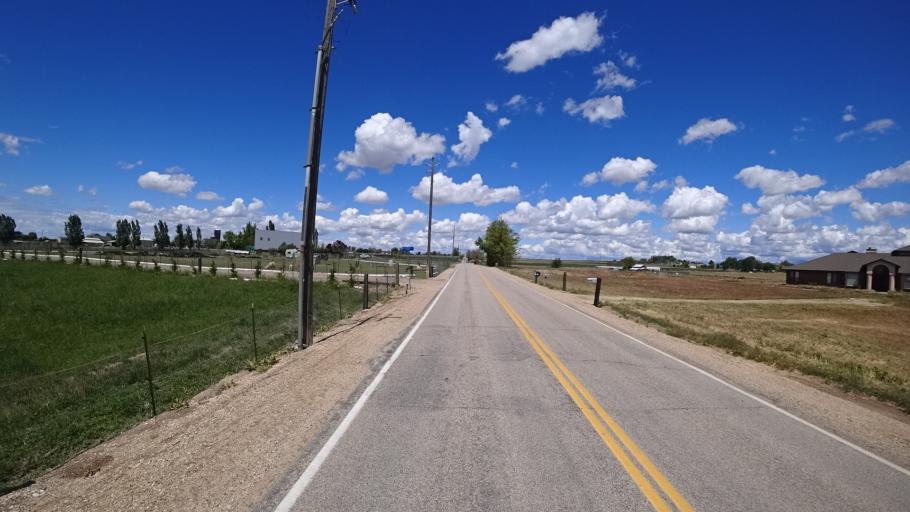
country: US
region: Idaho
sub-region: Ada County
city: Kuna
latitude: 43.5582
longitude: -116.4536
